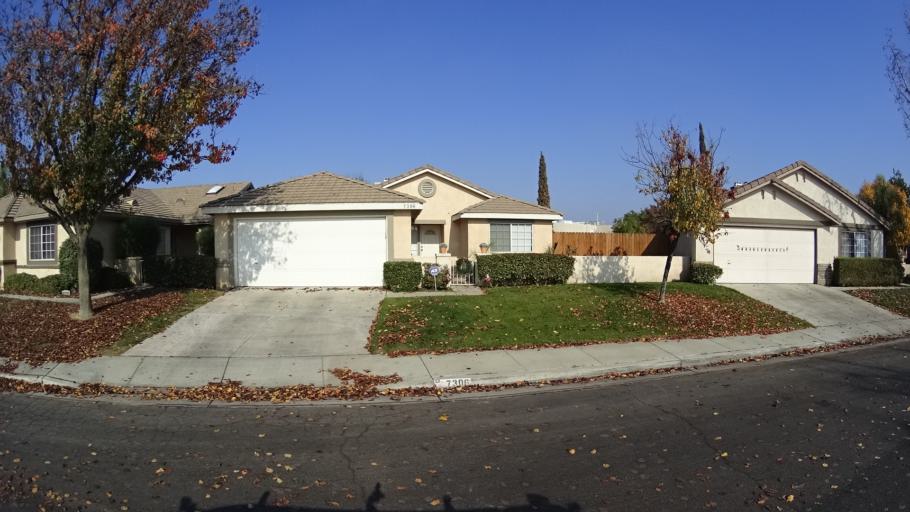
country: US
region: California
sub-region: Kern County
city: Greenacres
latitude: 35.3100
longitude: -119.0843
